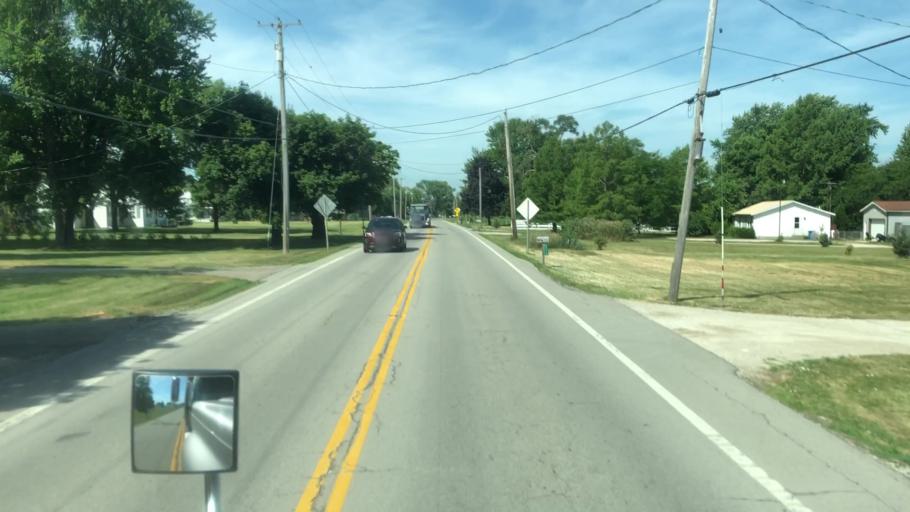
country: US
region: Ohio
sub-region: Erie County
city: Sandusky
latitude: 41.4370
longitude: -82.8254
